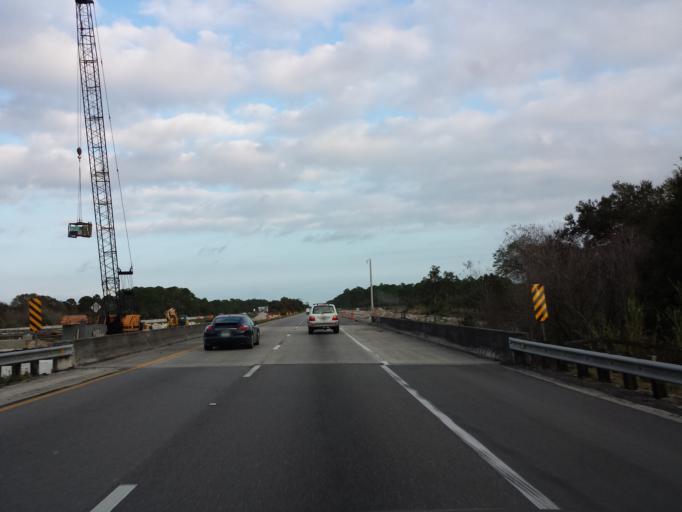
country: US
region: Florida
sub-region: Sarasota County
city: Warm Mineral Springs
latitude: 27.0999
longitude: -82.2719
